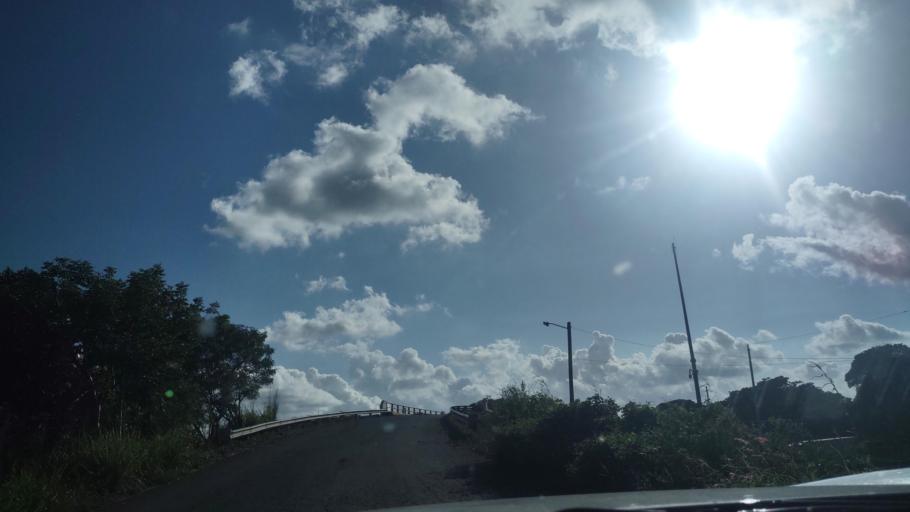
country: MX
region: Veracruz
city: El Tejar
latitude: 19.0649
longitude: -96.1757
